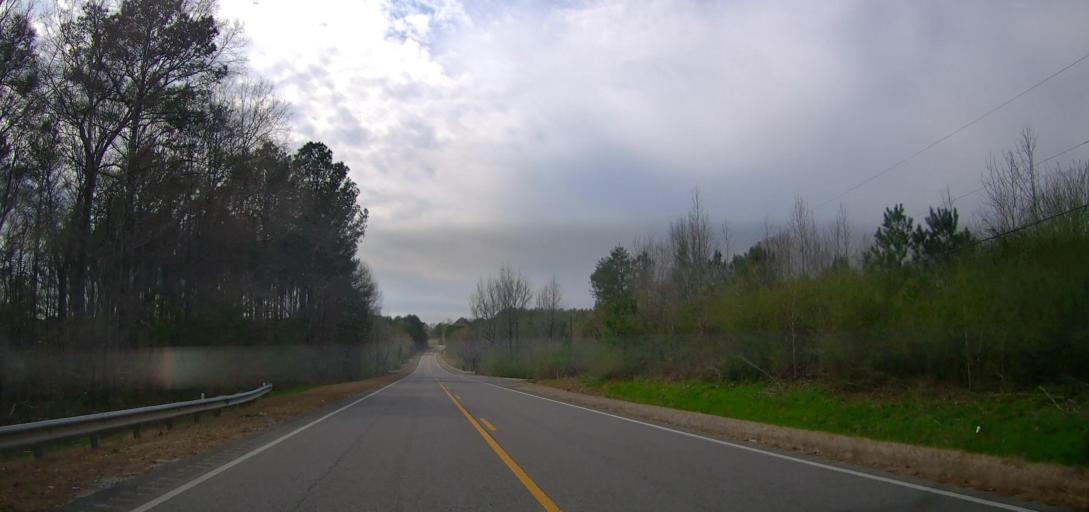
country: US
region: Alabama
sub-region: Walker County
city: Carbon Hill
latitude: 33.9176
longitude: -87.5722
